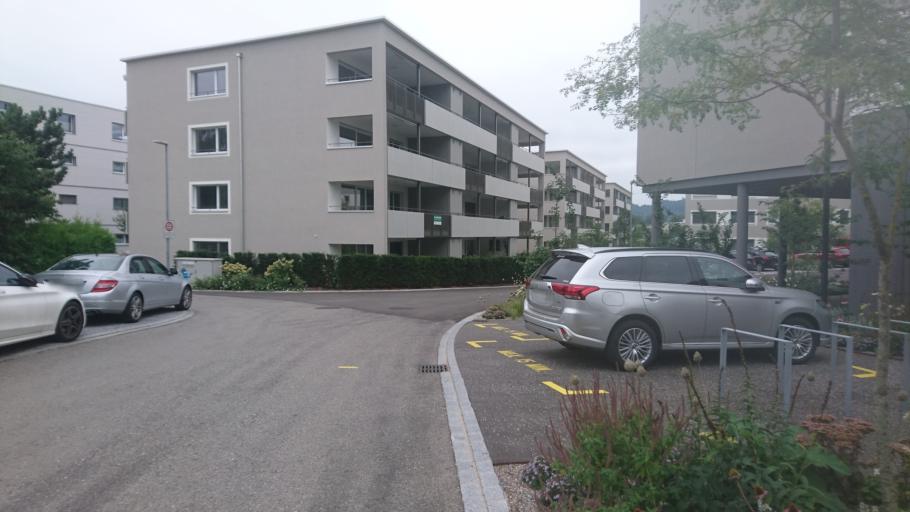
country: CH
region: Thurgau
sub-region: Muenchwilen District
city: Eschlikon
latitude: 47.4642
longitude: 8.9682
